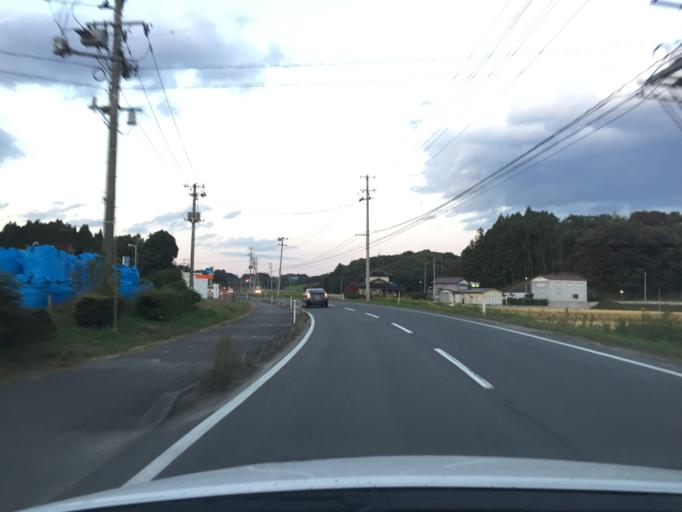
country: JP
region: Fukushima
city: Motomiya
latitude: 37.5004
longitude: 140.4563
